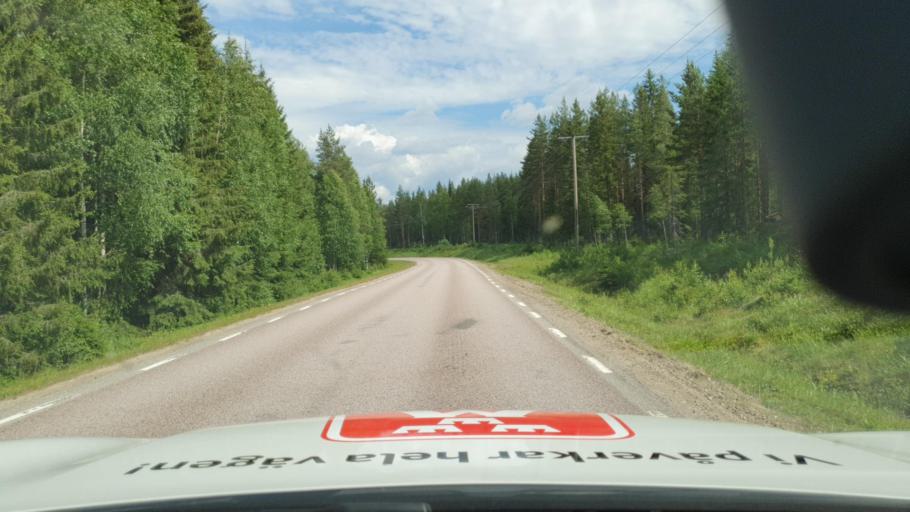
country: SE
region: Vaermland
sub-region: Torsby Kommun
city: Torsby
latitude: 60.7522
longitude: 12.7178
